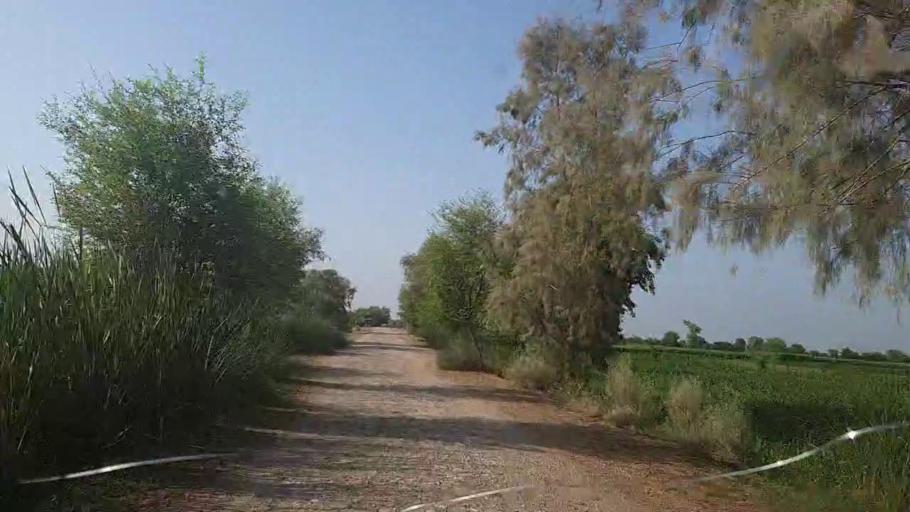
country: PK
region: Sindh
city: Khanpur
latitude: 27.7146
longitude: 69.3320
